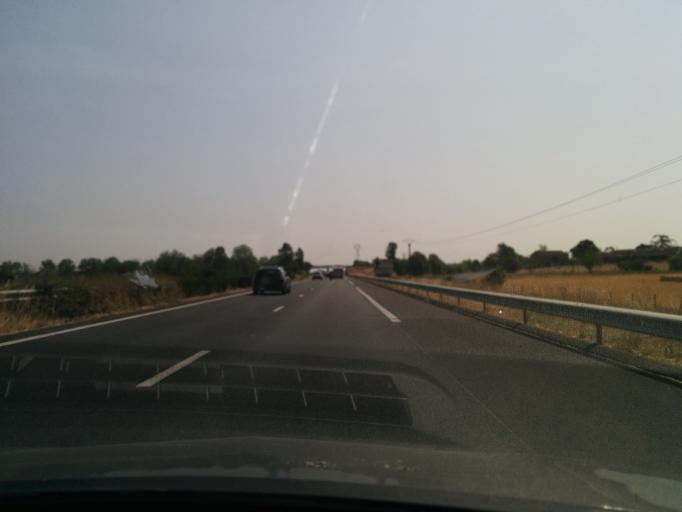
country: FR
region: Midi-Pyrenees
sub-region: Departement du Tarn
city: Brens
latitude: 43.8852
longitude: 1.9363
